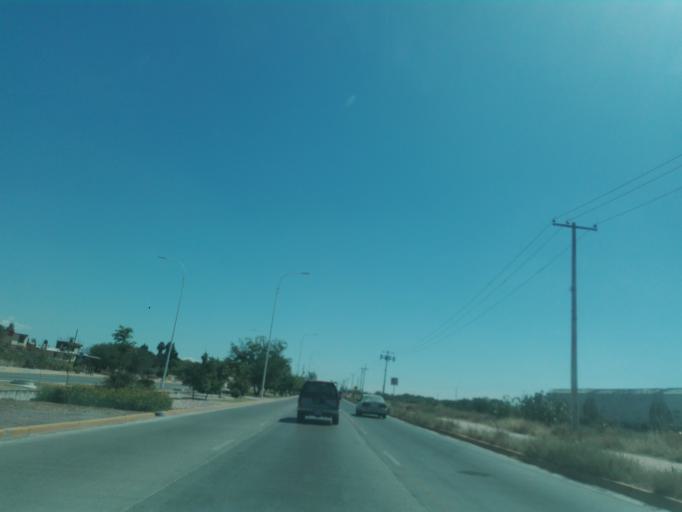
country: MX
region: Guanajuato
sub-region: Leon
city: San Jose de Duran (Los Troncoso)
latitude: 21.0834
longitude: -101.6645
